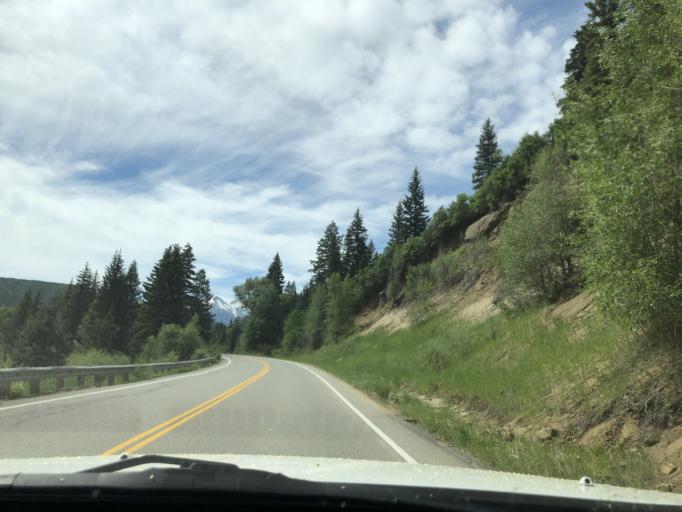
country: US
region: Colorado
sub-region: Delta County
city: Paonia
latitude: 38.9838
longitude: -107.3475
